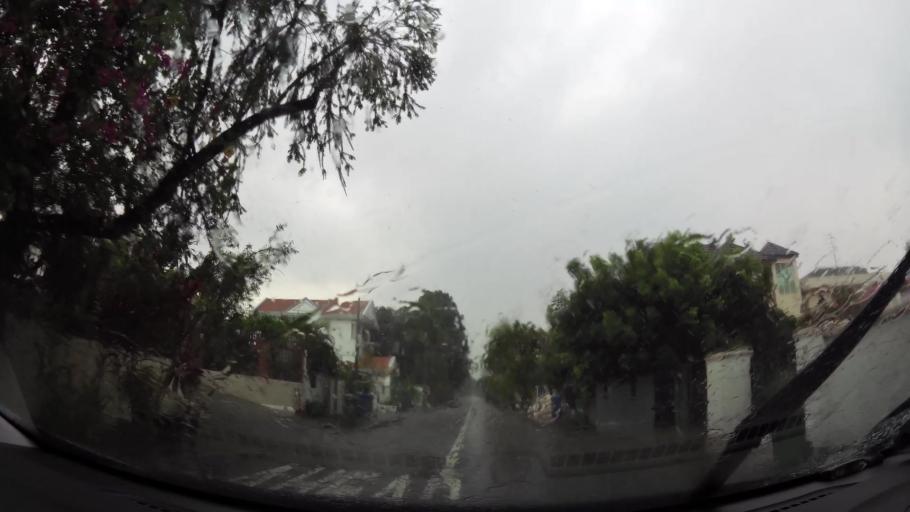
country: SG
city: Singapore
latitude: 1.3381
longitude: 103.9546
